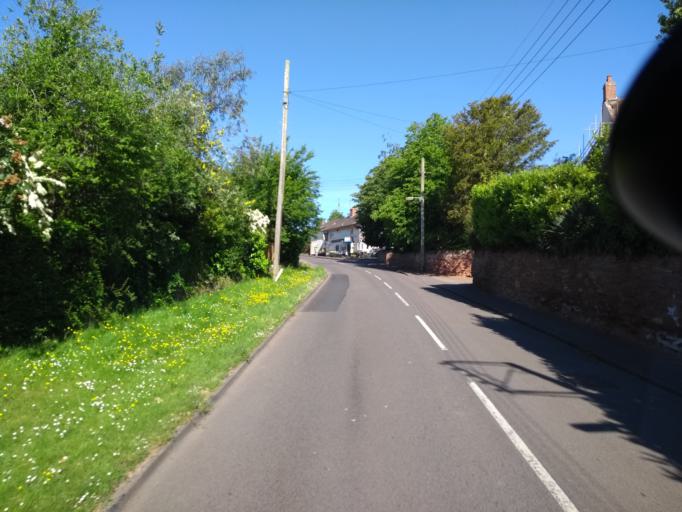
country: GB
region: England
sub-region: Somerset
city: Bridgwater
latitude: 51.1350
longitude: -3.0268
